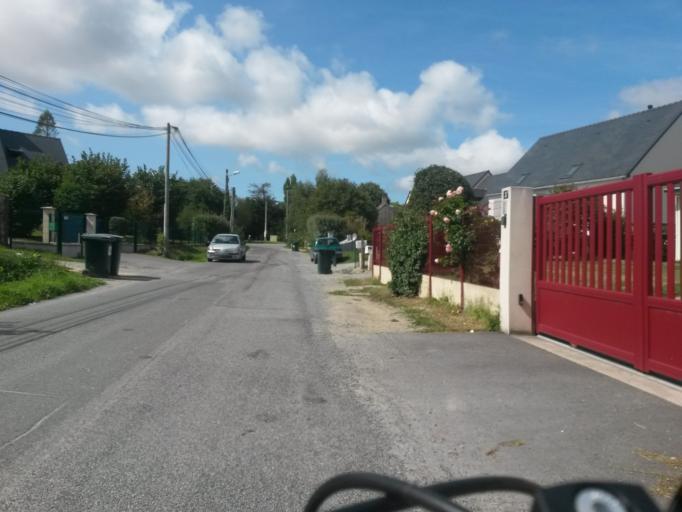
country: FR
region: Pays de la Loire
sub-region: Departement de la Loire-Atlantique
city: Saint-Molf
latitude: 47.3664
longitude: -2.3792
